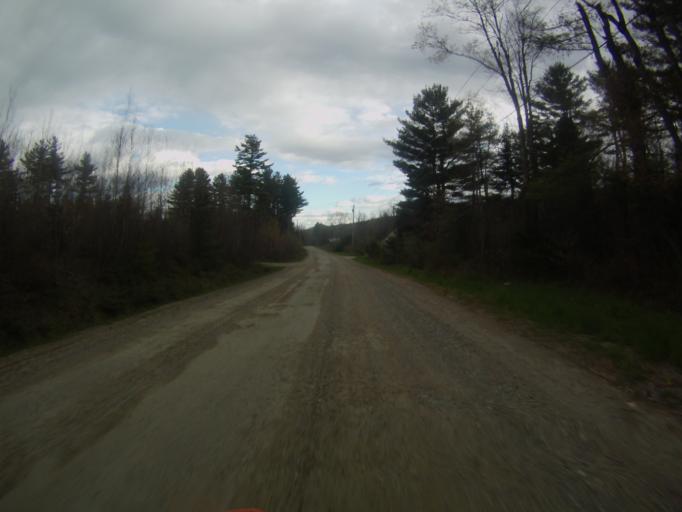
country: US
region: Vermont
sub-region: Addison County
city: Bristol
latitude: 44.0288
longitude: -73.0220
